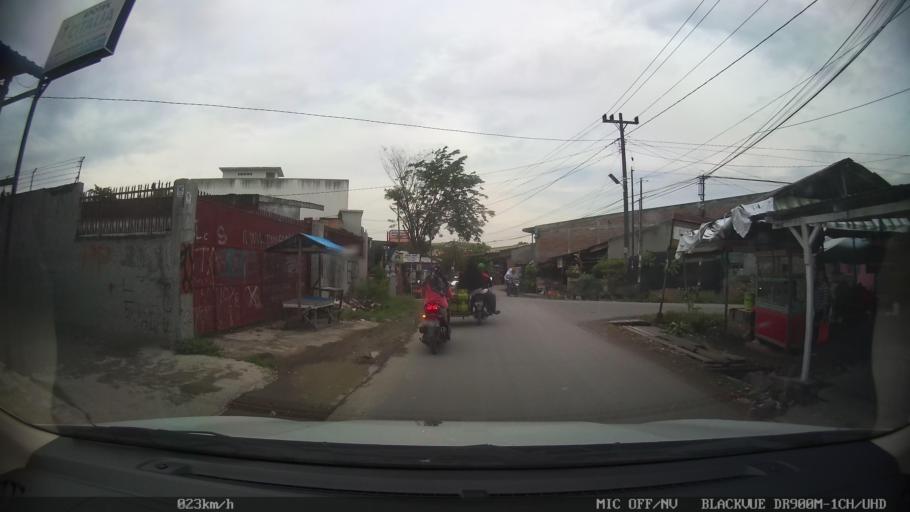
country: ID
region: North Sumatra
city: Sunggal
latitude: 3.6108
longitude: 98.6015
